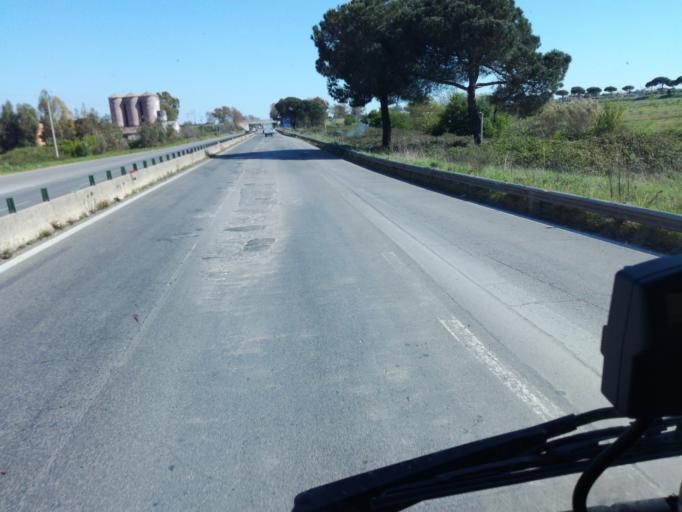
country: IT
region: Latium
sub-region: Provincia di Latina
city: Aprilia
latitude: 41.5716
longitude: 12.6645
